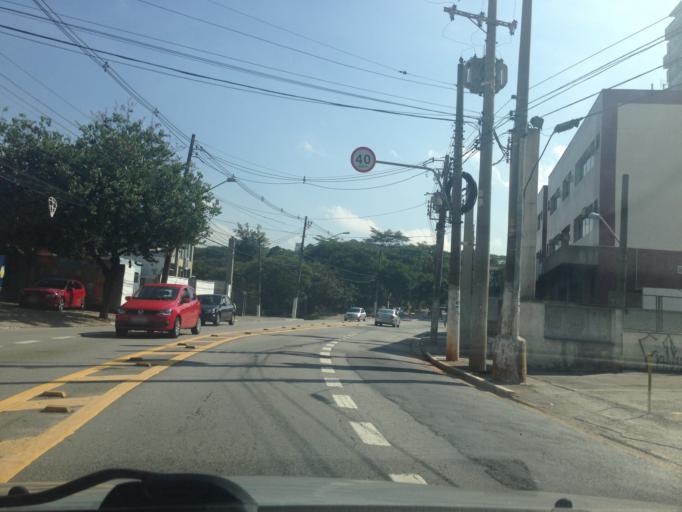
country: BR
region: Sao Paulo
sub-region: Sao Paulo
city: Sao Paulo
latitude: -23.5387
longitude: -46.7076
